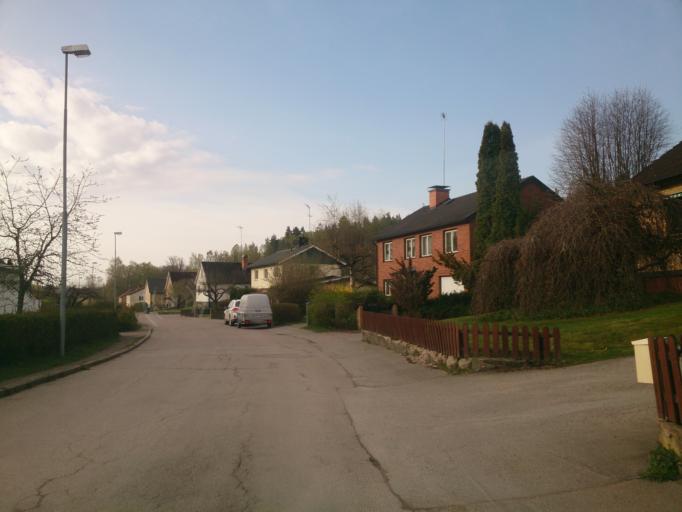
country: SE
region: OEstergoetland
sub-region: Atvidabergs Kommun
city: Atvidaberg
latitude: 58.2118
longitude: 16.0054
